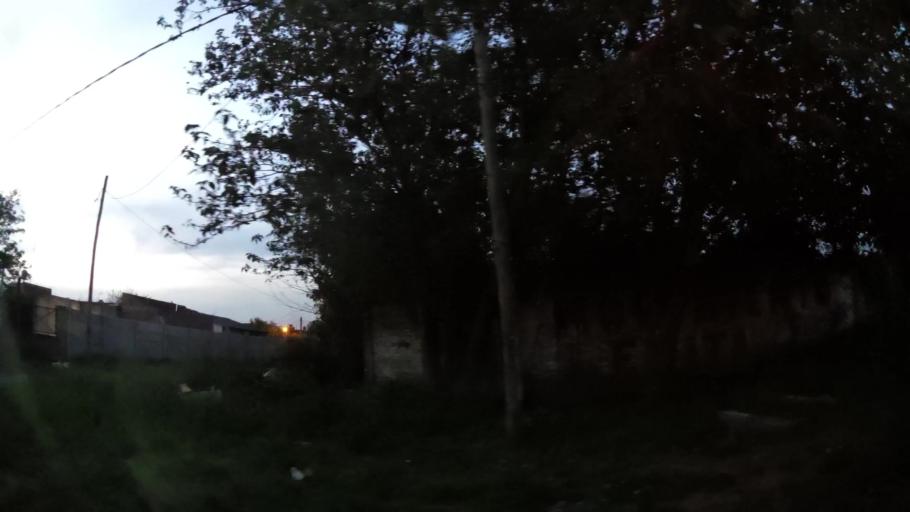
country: AR
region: Buenos Aires
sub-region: Partido de Quilmes
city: Quilmes
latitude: -34.8043
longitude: -58.2928
